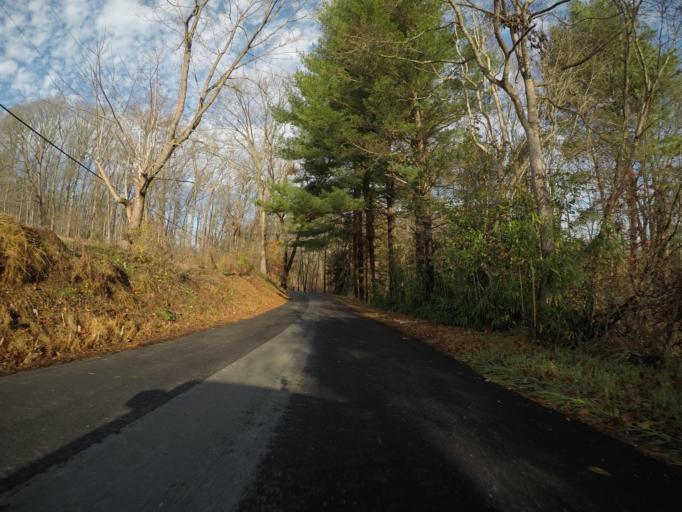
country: US
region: Maryland
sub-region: Carroll County
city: Hampstead
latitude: 39.5806
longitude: -76.8163
